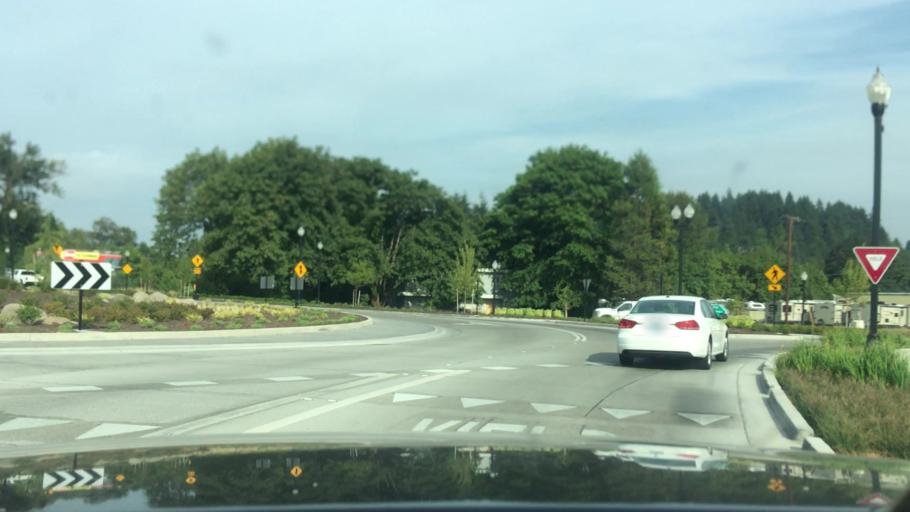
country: US
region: Oregon
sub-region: Lane County
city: Springfield
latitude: 44.0442
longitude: -123.0308
